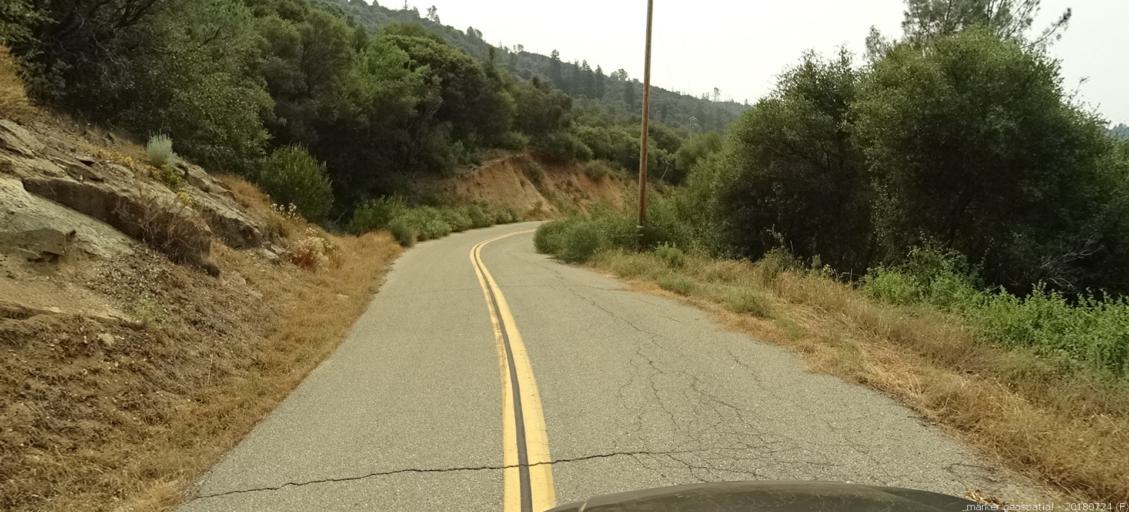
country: US
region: California
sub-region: Madera County
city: Oakhurst
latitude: 37.3427
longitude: -119.6045
